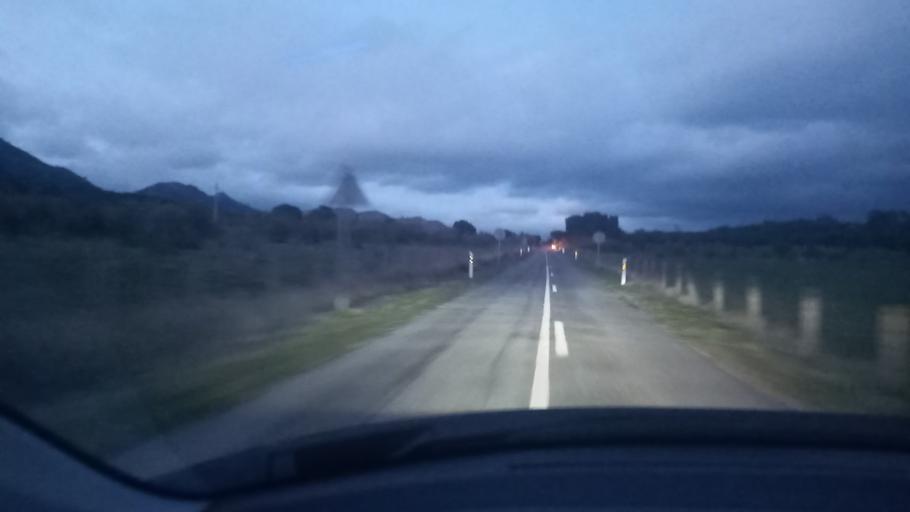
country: ES
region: Madrid
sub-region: Provincia de Madrid
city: Navas del Rey
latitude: 40.4333
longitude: -4.2463
